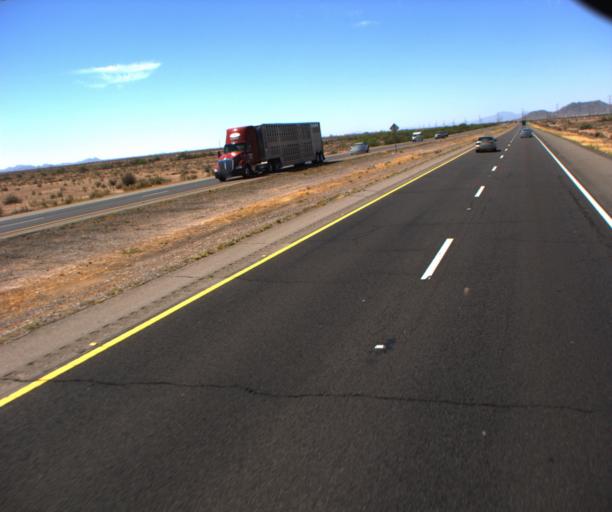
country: US
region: Arizona
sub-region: Maricopa County
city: Sun Lakes
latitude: 33.2134
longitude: -111.9910
